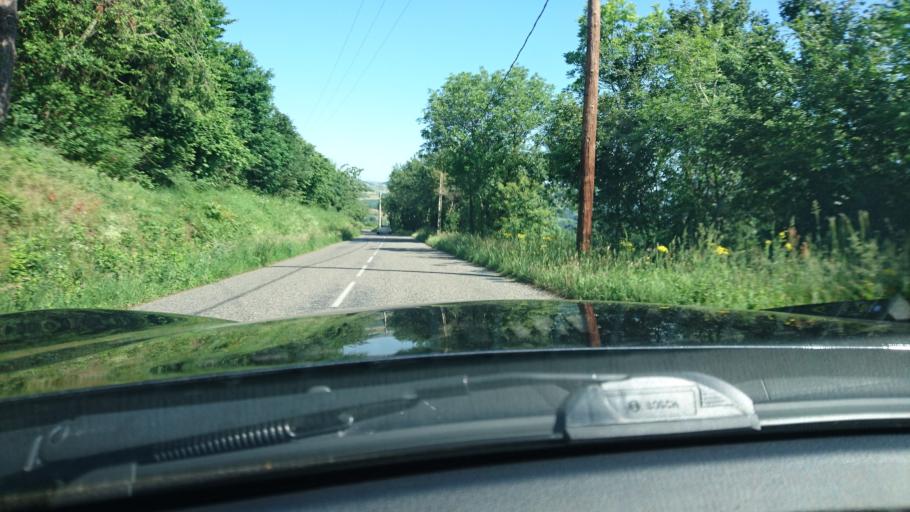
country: FR
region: Rhone-Alpes
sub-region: Departement du Rhone
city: Saint-Pierre-la-Palud
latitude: 45.7785
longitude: 4.5883
